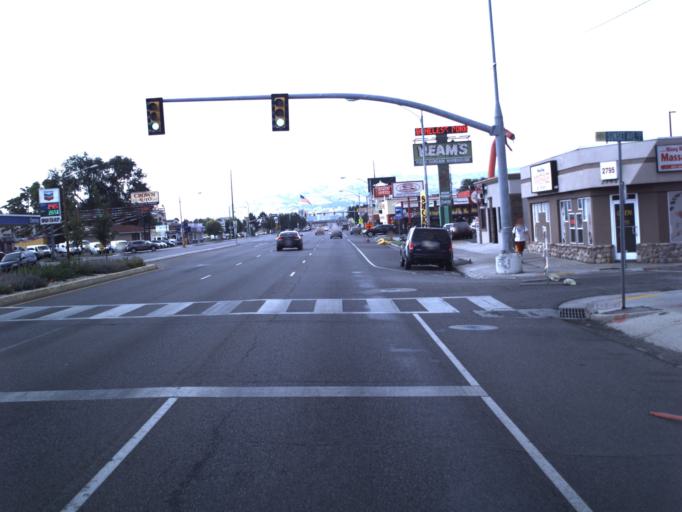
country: US
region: Utah
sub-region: Salt Lake County
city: South Salt Lake
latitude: 40.7098
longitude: -111.8882
